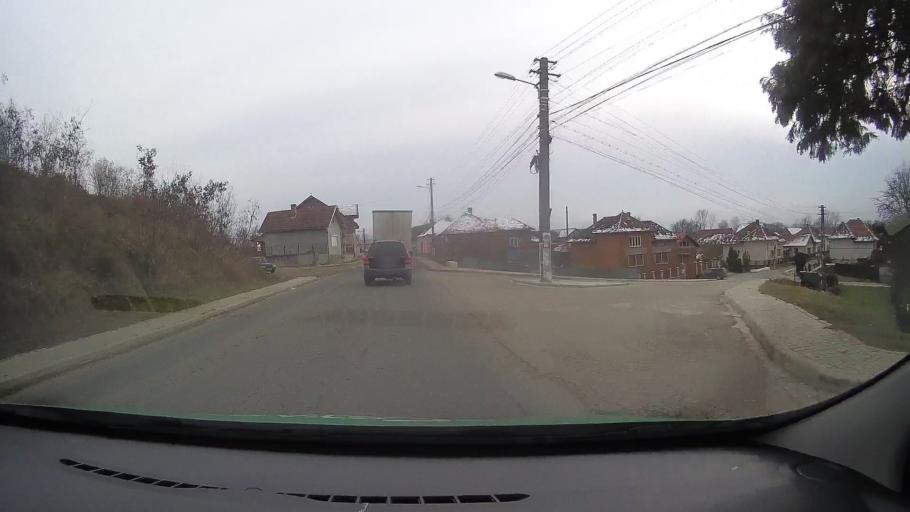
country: RO
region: Hunedoara
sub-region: Comuna Geoagiu
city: Geoagiu
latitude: 45.9066
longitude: 23.2122
